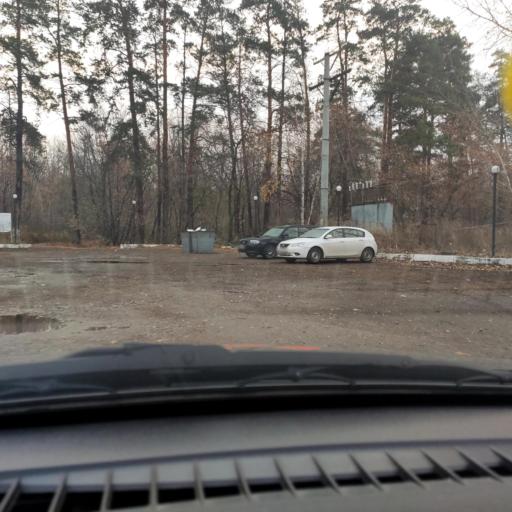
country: RU
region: Samara
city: Tol'yatti
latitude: 53.5230
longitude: 49.3348
